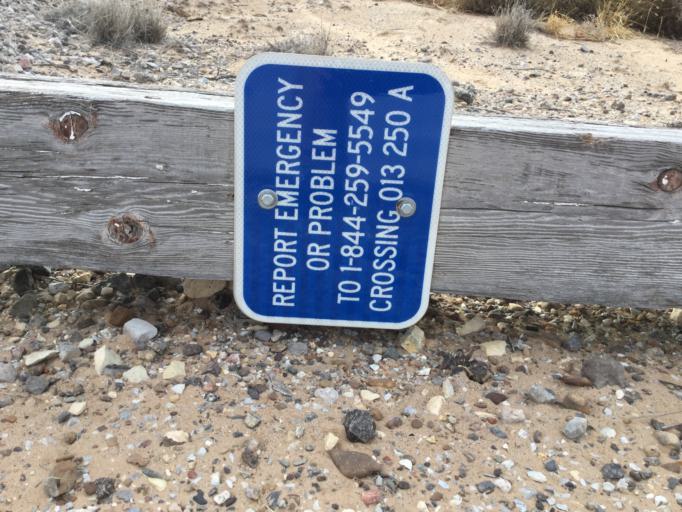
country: US
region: Kansas
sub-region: Morton County
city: Elkhart
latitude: 37.0275
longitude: -101.8631
